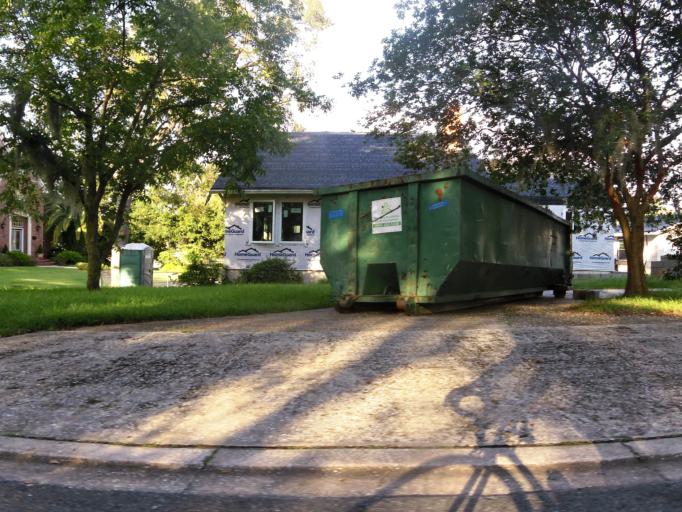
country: US
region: Florida
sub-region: Duval County
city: Jacksonville
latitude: 30.3091
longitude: -81.6304
